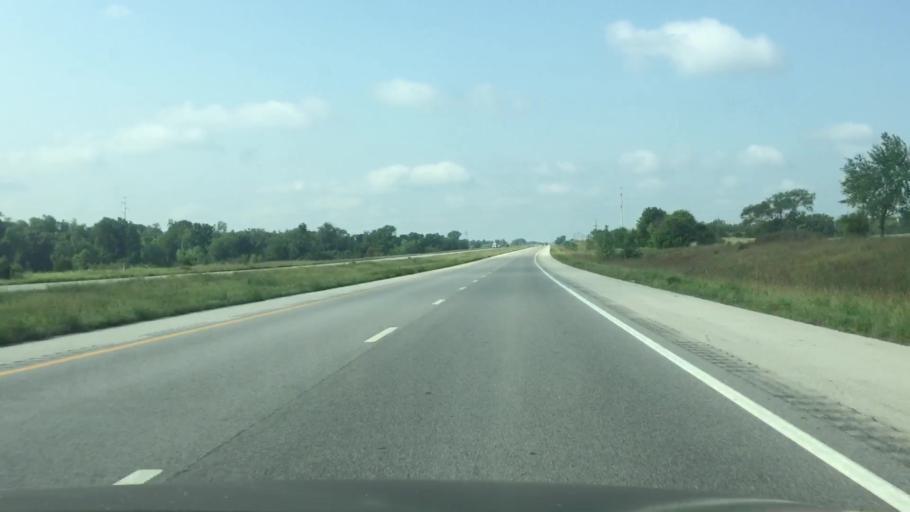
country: US
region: Kansas
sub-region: Miami County
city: Paola
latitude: 38.5478
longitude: -94.8768
